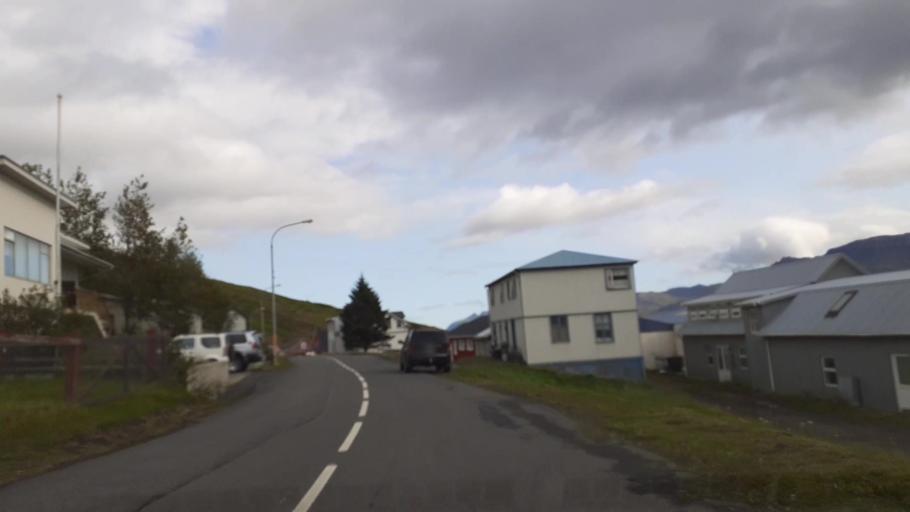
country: IS
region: East
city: Eskifjoerdur
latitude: 65.0654
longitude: -14.0019
